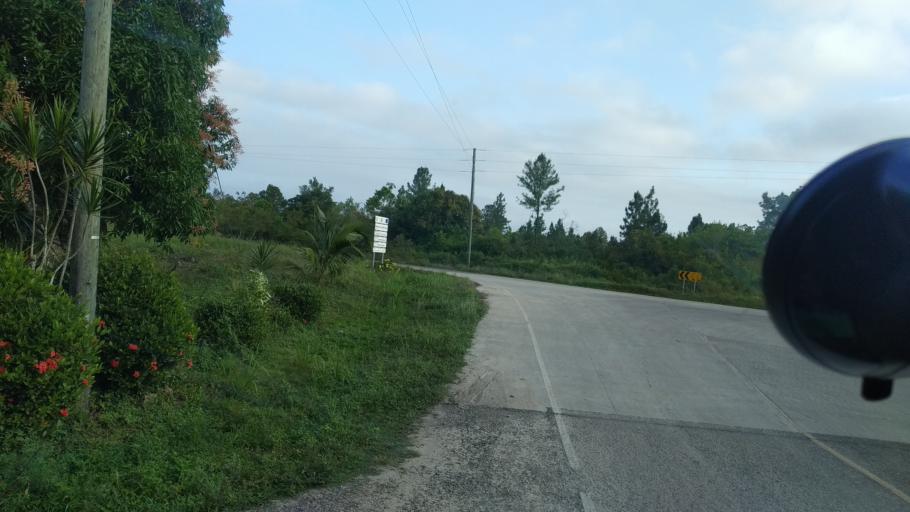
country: BZ
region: Stann Creek
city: Placencia
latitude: 16.5745
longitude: -88.5298
